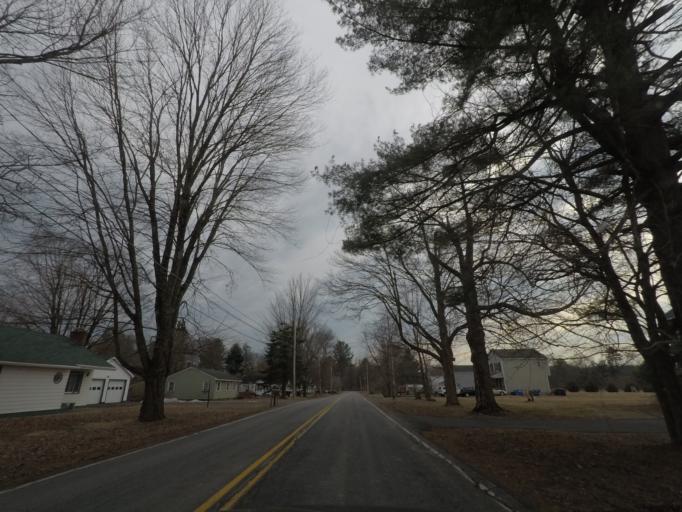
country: US
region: New York
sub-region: Saratoga County
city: Schuylerville
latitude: 43.1196
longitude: -73.5723
